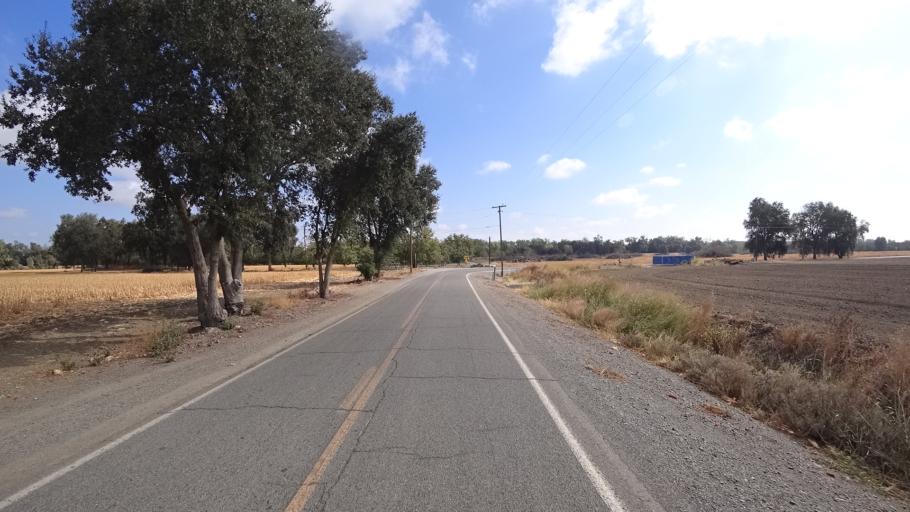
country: US
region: California
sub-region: Yolo County
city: Woodland
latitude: 38.7956
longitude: -121.7014
